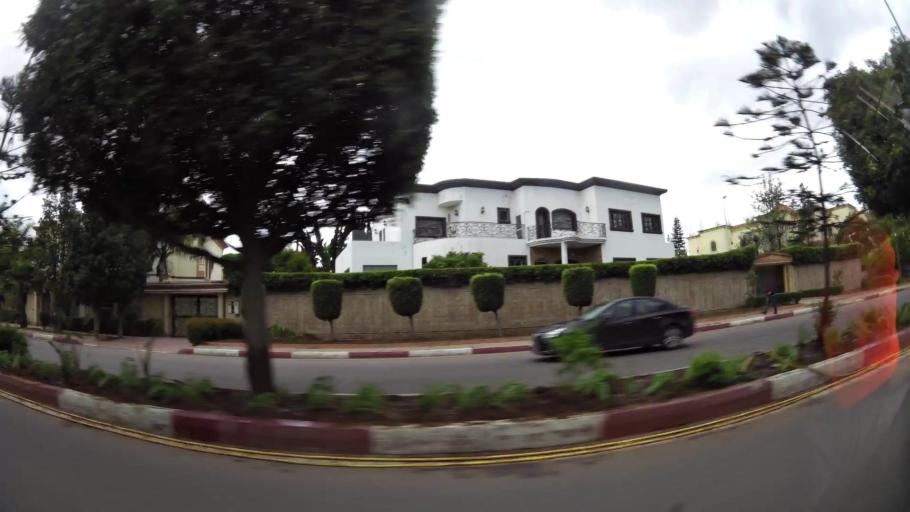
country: MA
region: Grand Casablanca
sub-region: Casablanca
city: Casablanca
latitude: 33.5330
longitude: -7.6297
